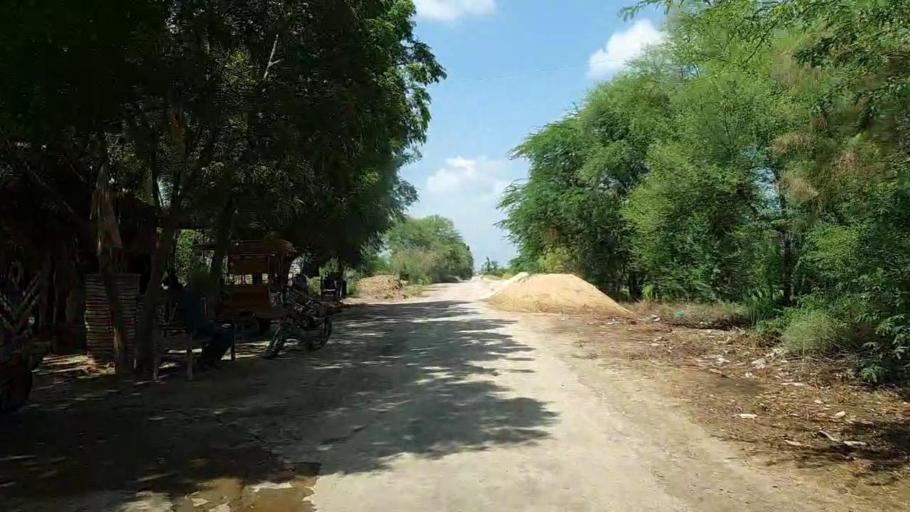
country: PK
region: Sindh
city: Kandiaro
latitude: 27.0223
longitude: 68.2720
